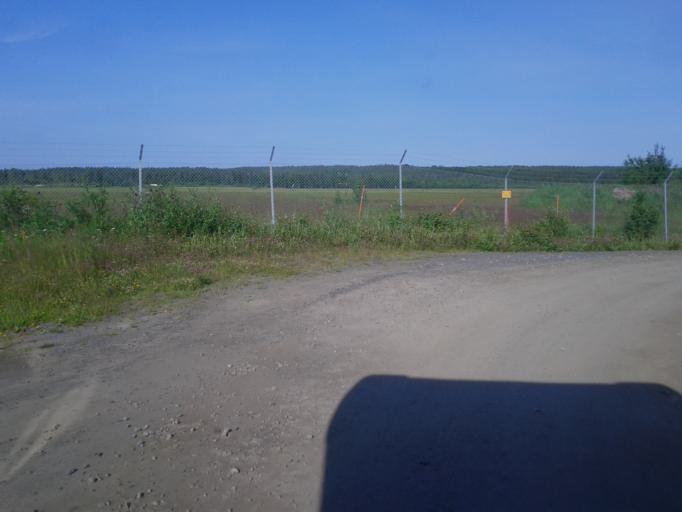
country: SE
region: Vaesterbotten
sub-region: Umea Kommun
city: Umea
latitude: 63.7823
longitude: 20.2945
